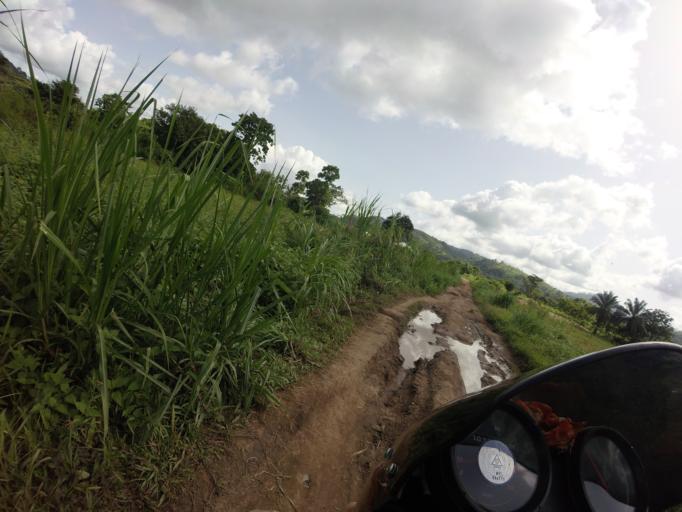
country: SL
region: Eastern Province
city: Tombu
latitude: 8.6013
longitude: -10.6990
